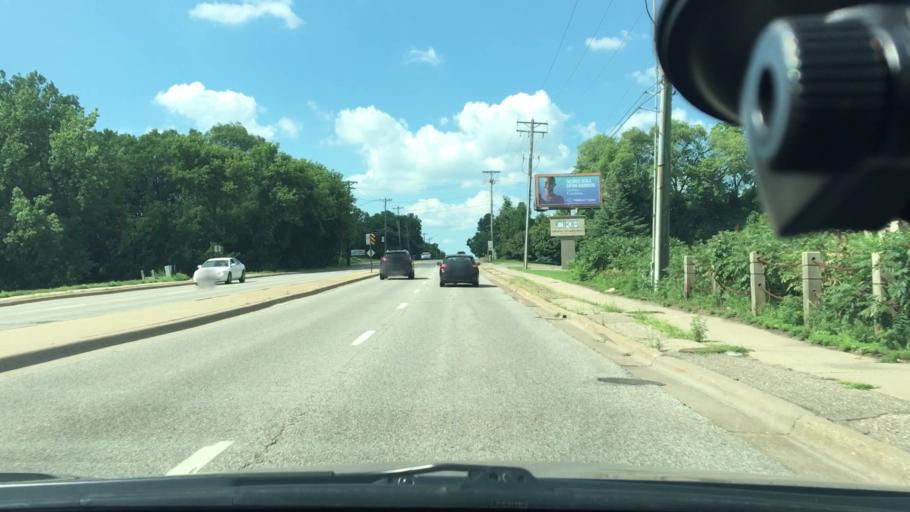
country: US
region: Minnesota
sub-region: Hennepin County
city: New Hope
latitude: 45.0227
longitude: -93.3801
